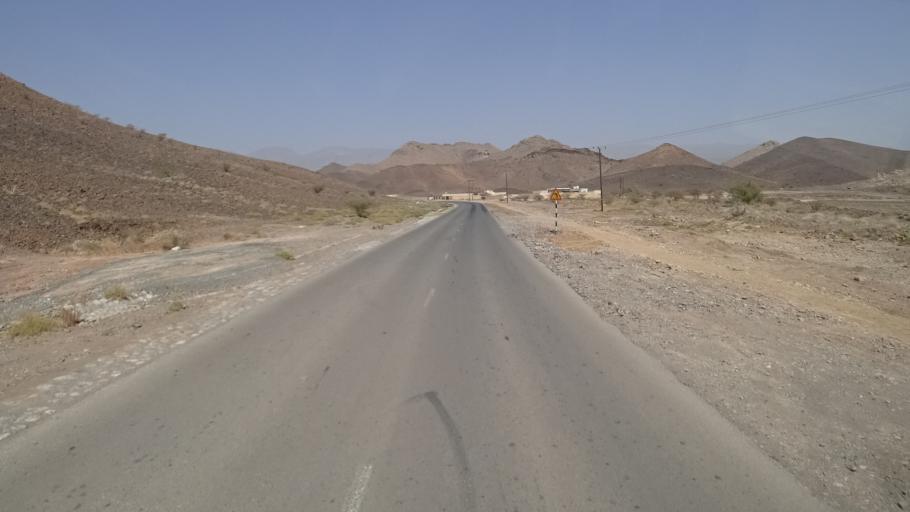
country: OM
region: Muhafazat ad Dakhiliyah
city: Bahla'
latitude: 23.0632
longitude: 57.3203
